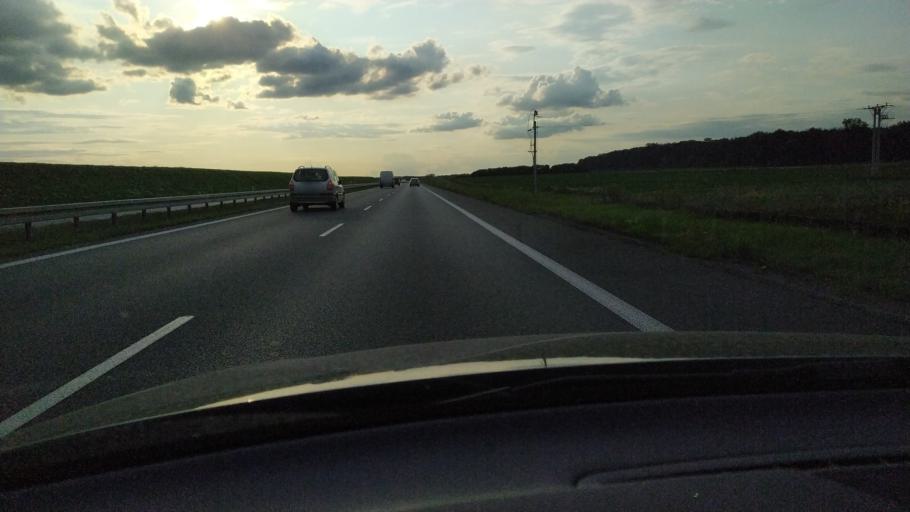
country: PL
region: Lower Silesian Voivodeship
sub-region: Powiat wroclawski
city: Mirkow
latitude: 51.1777
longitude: 17.1237
